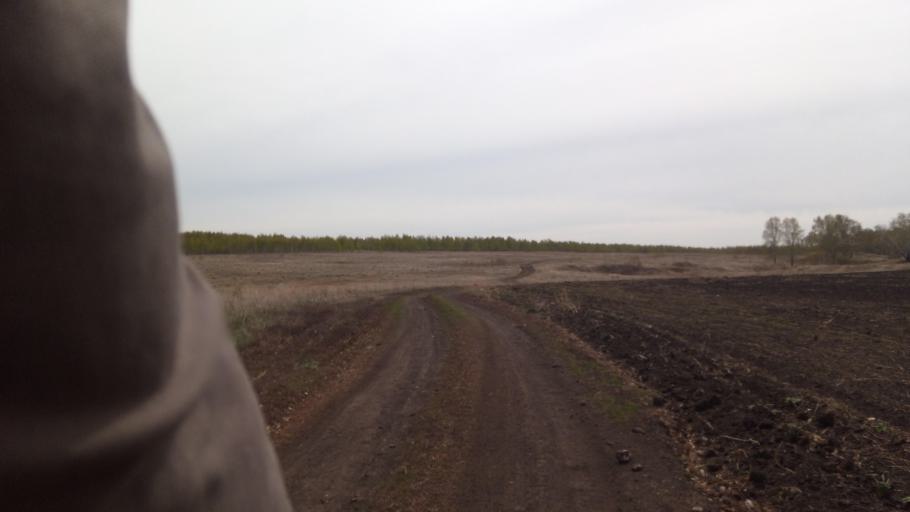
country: RU
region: Chelyabinsk
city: Timiryazevskiy
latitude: 55.0149
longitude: 60.8583
